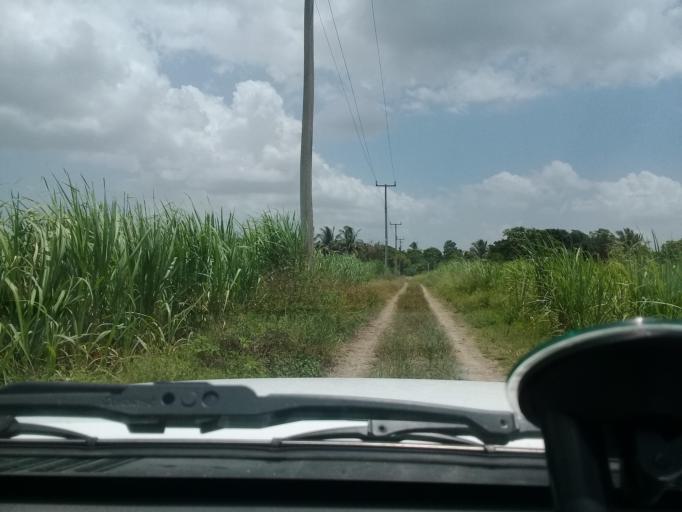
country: MX
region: Veracruz
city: Moralillo
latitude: 22.1364
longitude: -98.0404
